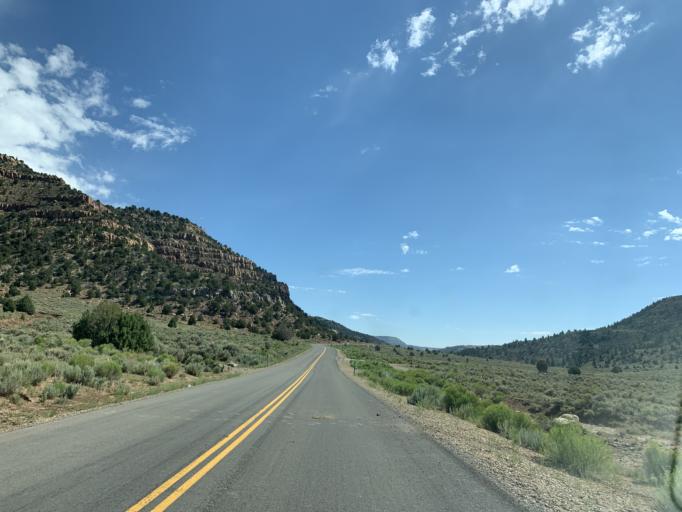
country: US
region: Utah
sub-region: Carbon County
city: East Carbon City
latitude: 39.7417
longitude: -110.5624
